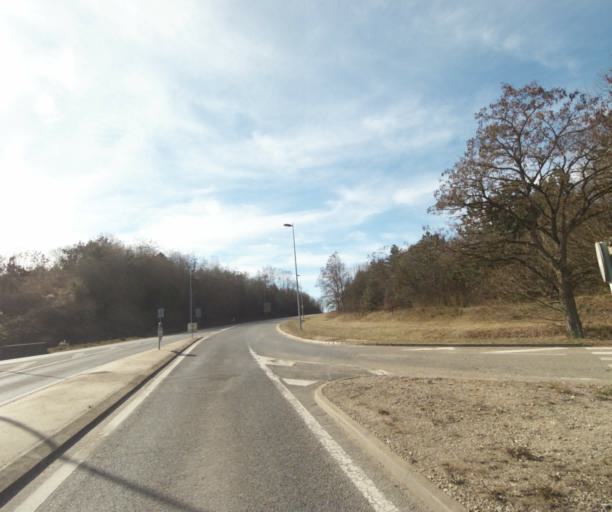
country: FR
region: Lorraine
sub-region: Departement de Meurthe-et-Moselle
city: Maxeville
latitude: 48.7099
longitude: 6.1459
